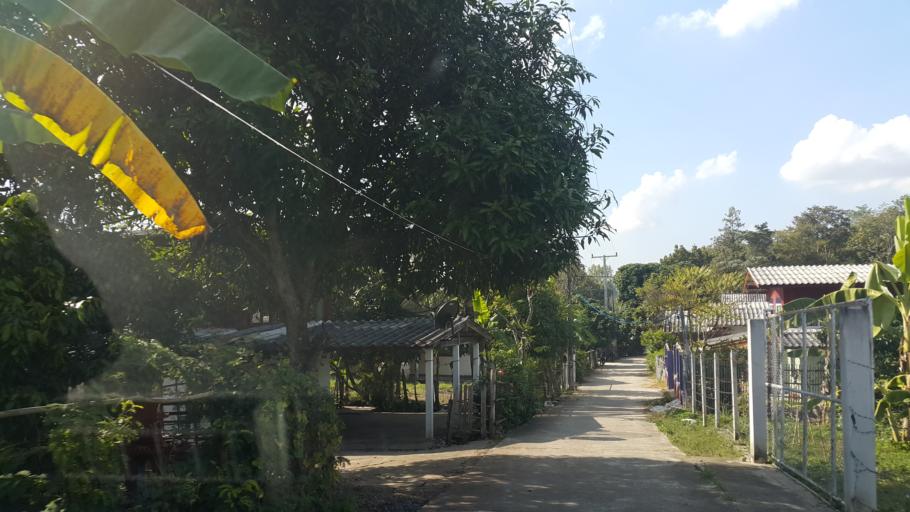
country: TH
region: Lamphun
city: Ban Thi
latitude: 18.5887
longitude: 99.1590
